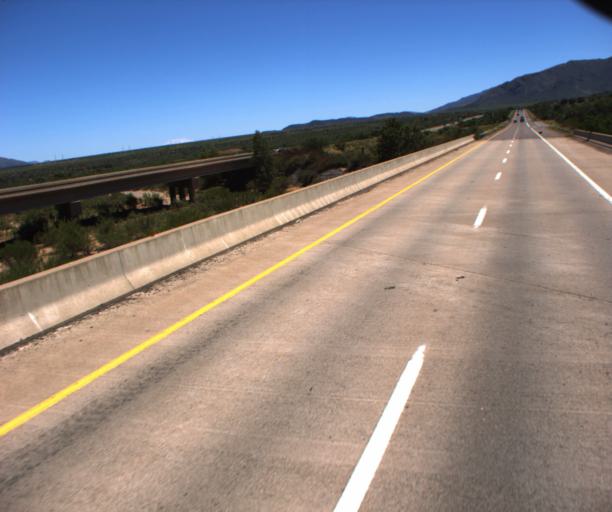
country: US
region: Arizona
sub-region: Gila County
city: Payson
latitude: 34.0870
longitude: -111.3550
